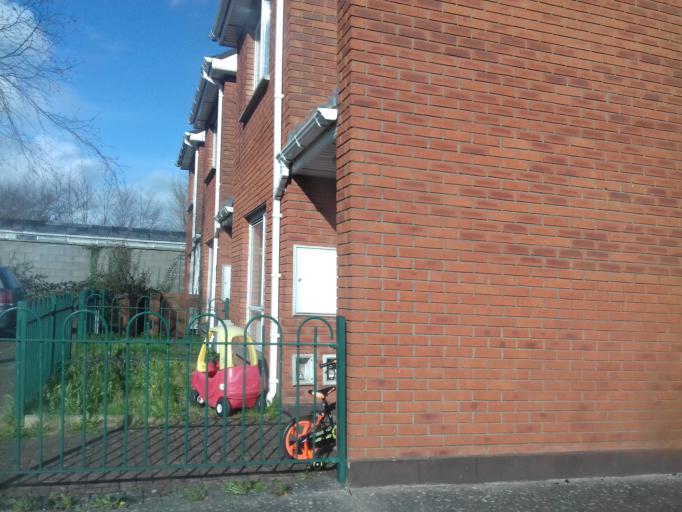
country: IE
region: Leinster
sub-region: Fingal County
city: Blanchardstown
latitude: 53.4051
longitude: -6.3929
